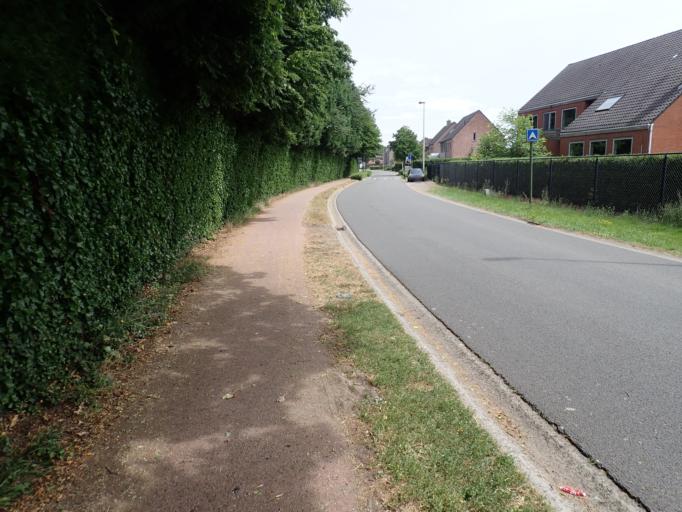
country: BE
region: Flanders
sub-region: Provincie Antwerpen
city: Rijkevorsel
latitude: 51.3326
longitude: 4.7787
